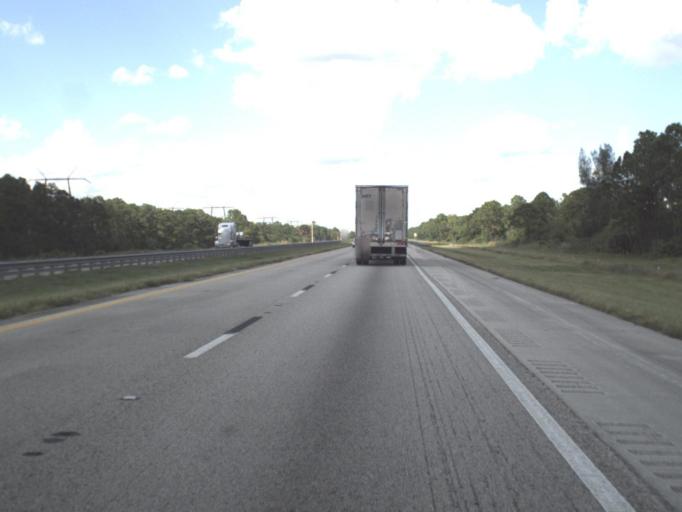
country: US
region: Florida
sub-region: Indian River County
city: West Vero Corridor
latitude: 27.5173
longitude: -80.5944
